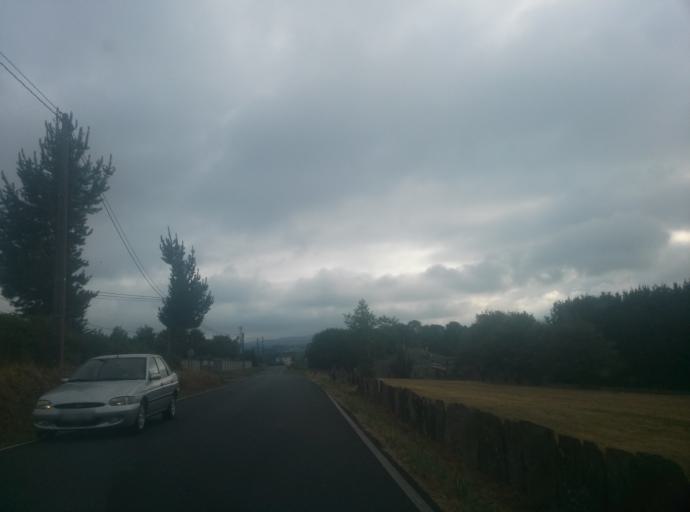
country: ES
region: Galicia
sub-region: Provincia de Lugo
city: Lugo
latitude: 43.0650
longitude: -7.5608
